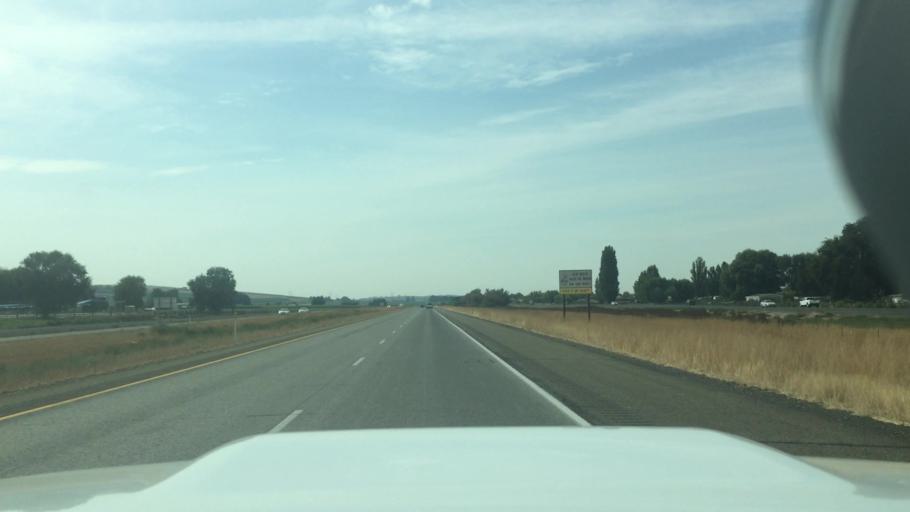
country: US
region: Washington
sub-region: Yakima County
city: Sunnyside
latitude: 46.3294
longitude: -120.0932
